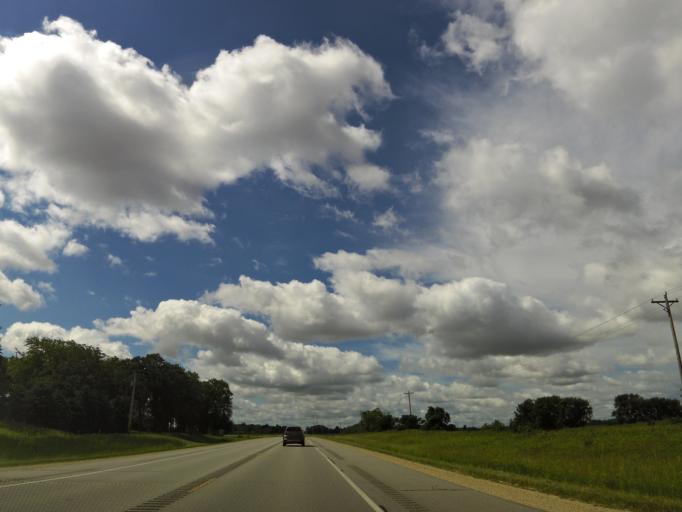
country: US
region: Minnesota
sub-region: Olmsted County
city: Stewartville
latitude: 43.8295
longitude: -92.4896
